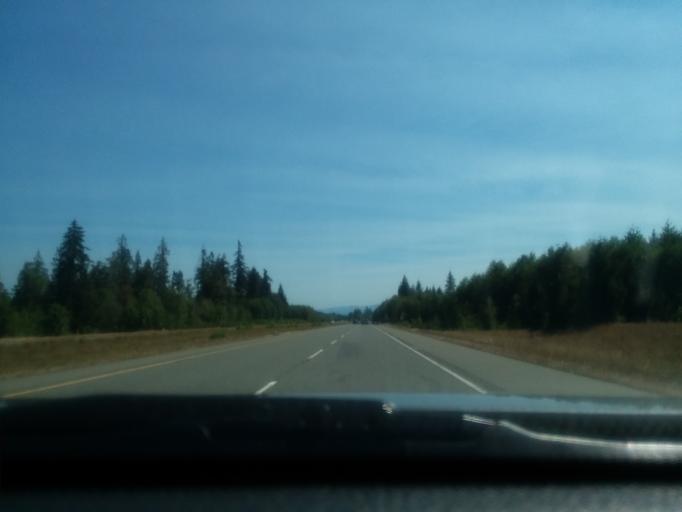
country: CA
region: British Columbia
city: Cumberland
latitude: 49.5245
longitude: -124.8603
